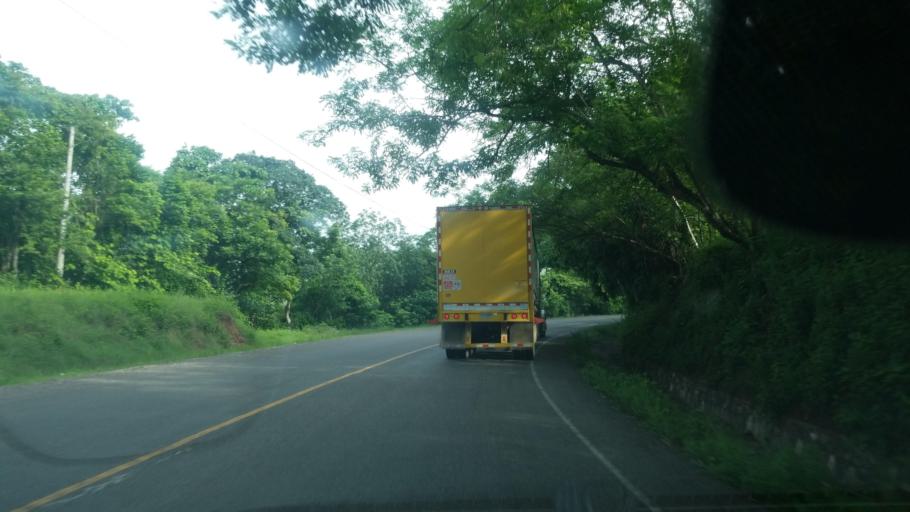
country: HN
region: Santa Barbara
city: Ilama
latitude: 15.0717
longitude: -88.2242
